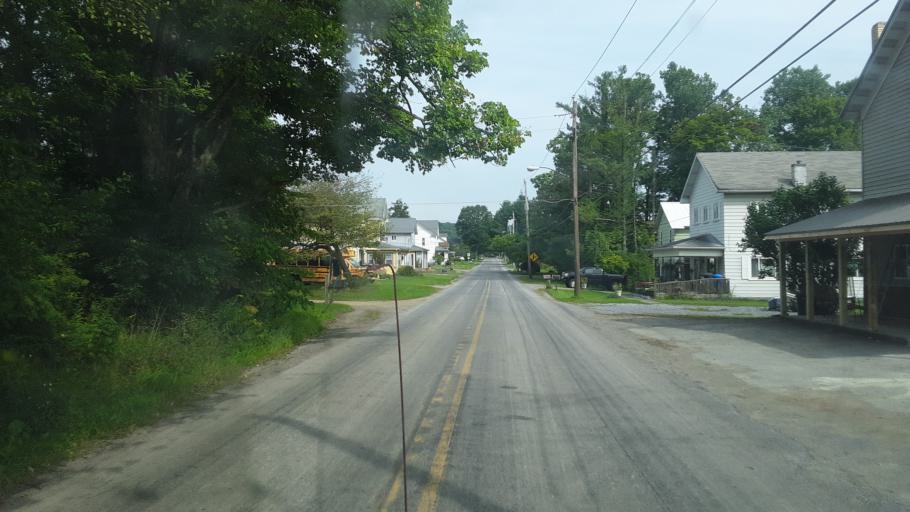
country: US
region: Pennsylvania
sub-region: Jefferson County
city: Punxsutawney
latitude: 40.9122
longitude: -79.0450
